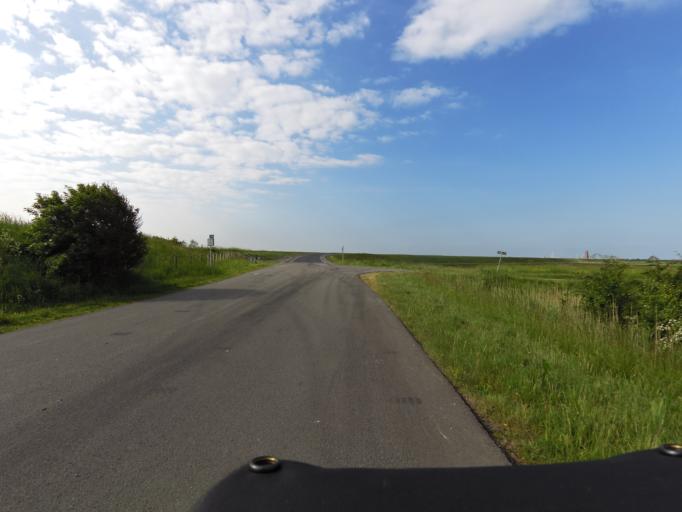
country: NL
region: Zeeland
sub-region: Schouwen-Duiveland
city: Haamstede
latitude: 51.6891
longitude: 3.7859
